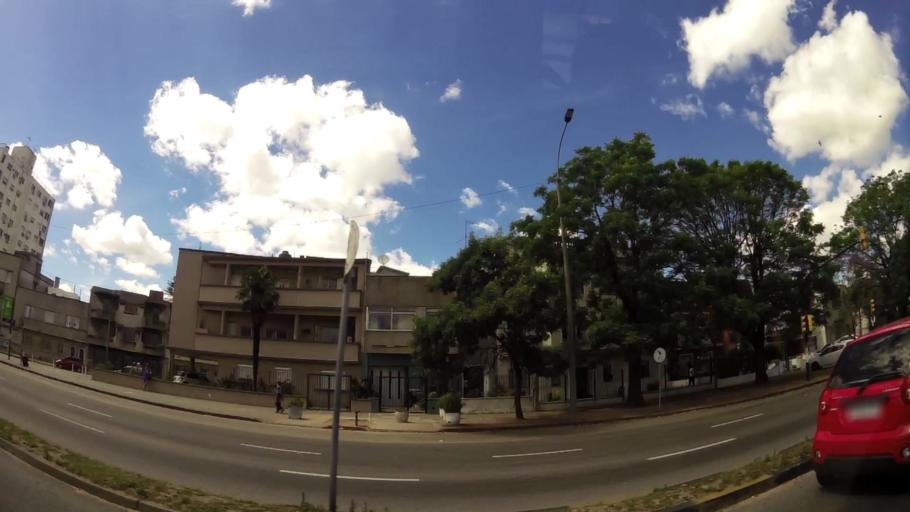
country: UY
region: Montevideo
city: Montevideo
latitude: -34.8725
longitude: -56.2033
